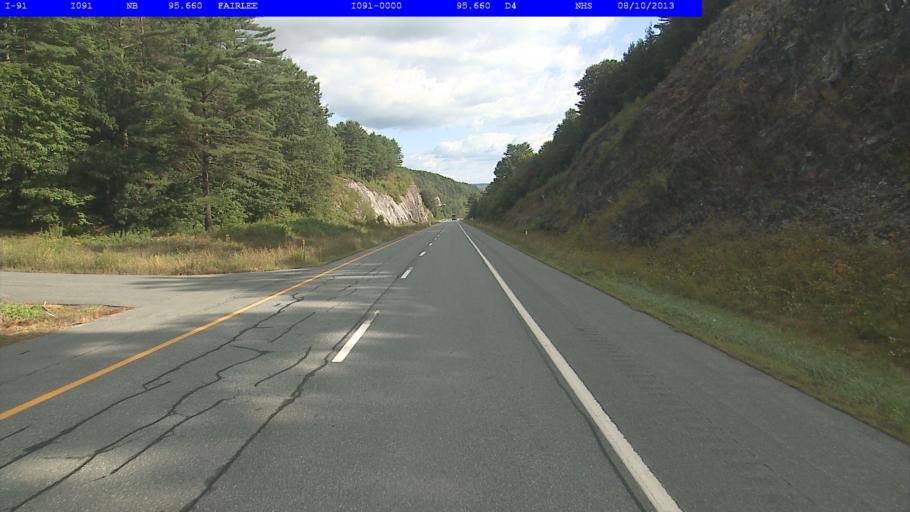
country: US
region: New Hampshire
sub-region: Grafton County
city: Orford
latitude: 43.9568
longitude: -72.1292
